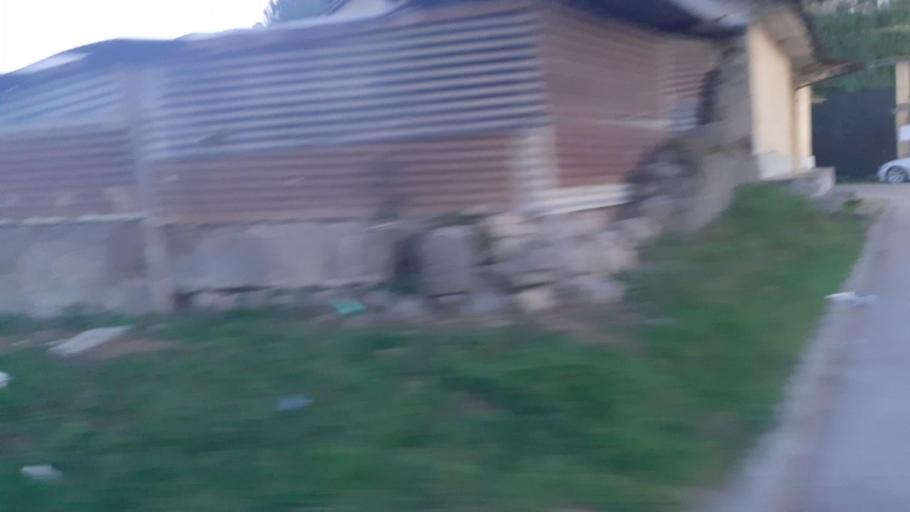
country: GT
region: Quetzaltenango
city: Quetzaltenango
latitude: 14.8277
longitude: -91.5313
